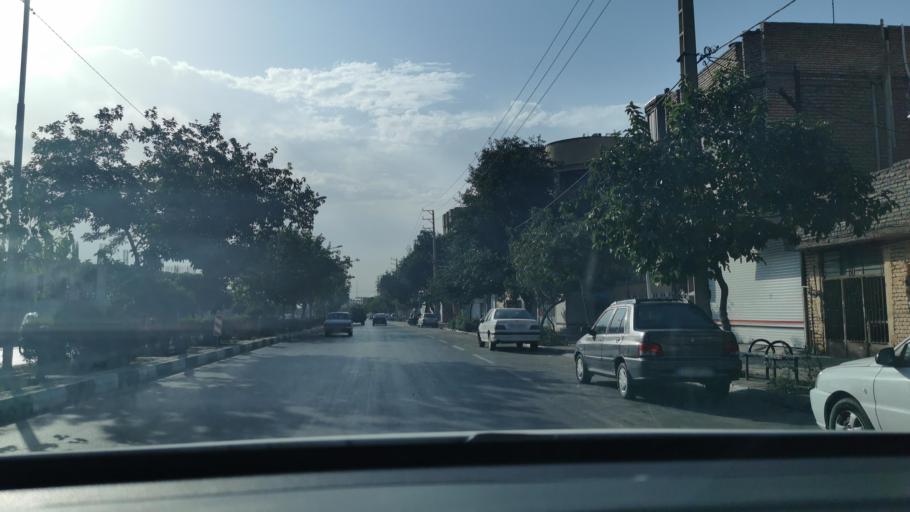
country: IR
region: Razavi Khorasan
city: Mashhad
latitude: 36.2898
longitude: 59.6511
